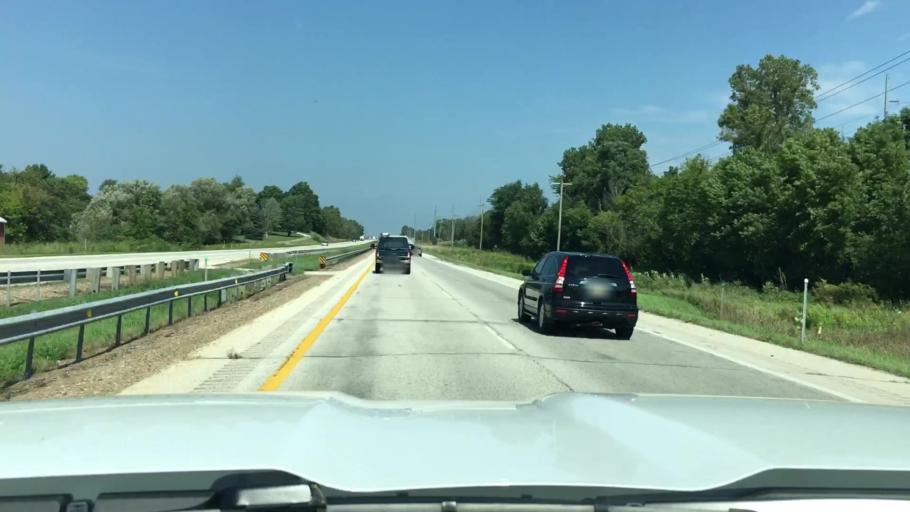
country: US
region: Michigan
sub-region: Kalamazoo County
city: Schoolcraft
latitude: 42.0545
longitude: -85.6357
